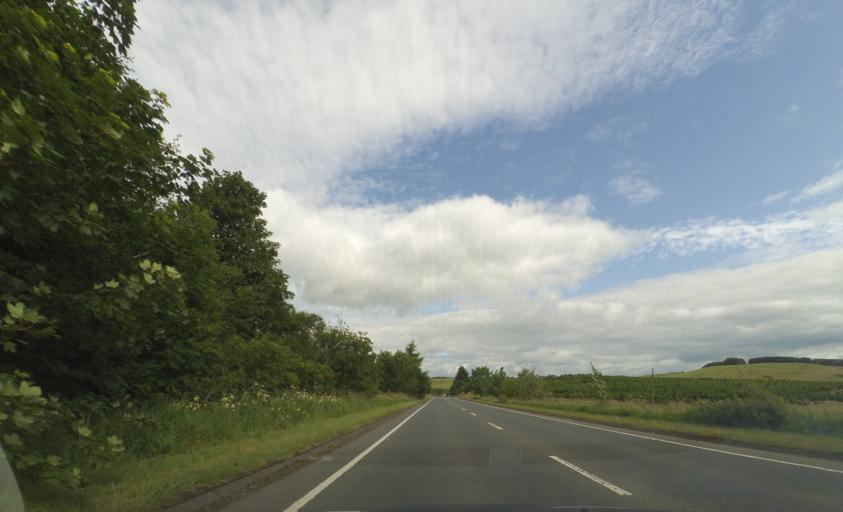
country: GB
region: Scotland
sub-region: The Scottish Borders
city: Selkirk
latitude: 55.5271
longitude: -2.8260
